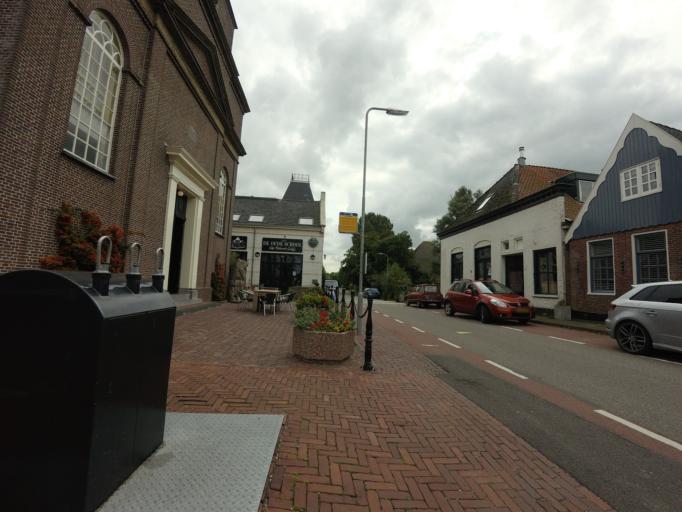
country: NL
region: North Holland
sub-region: Gemeente Edam-Volendam
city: Edam
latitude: 52.5644
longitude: 5.0299
